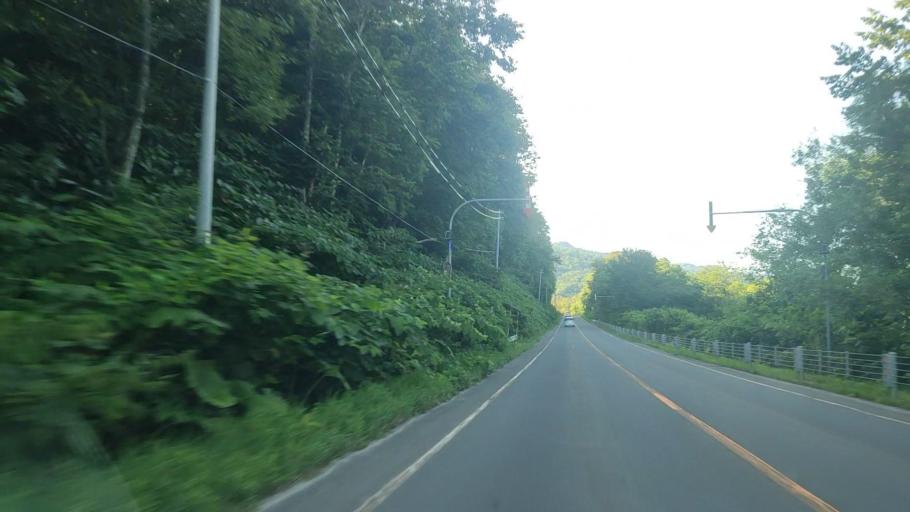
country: JP
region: Hokkaido
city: Nayoro
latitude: 44.7352
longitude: 142.1904
